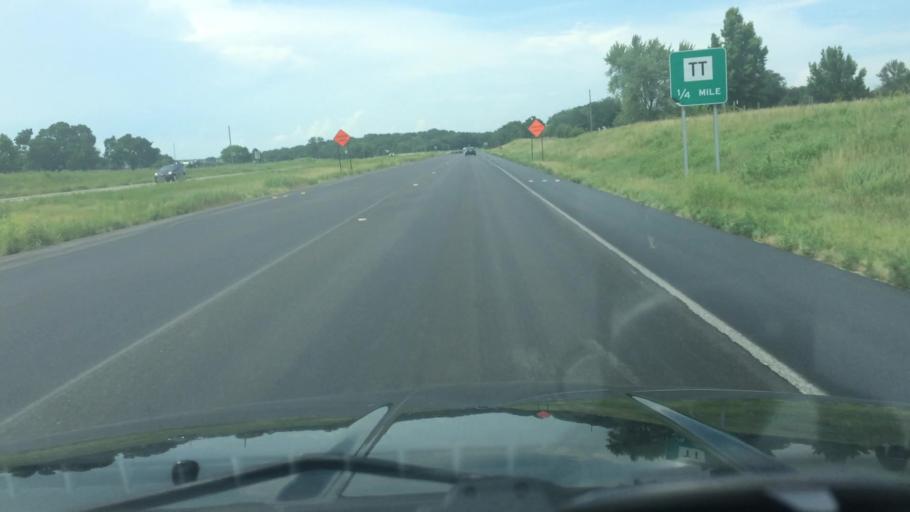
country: US
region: Missouri
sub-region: Saint Clair County
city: Osceola
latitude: 38.0064
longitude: -93.6565
